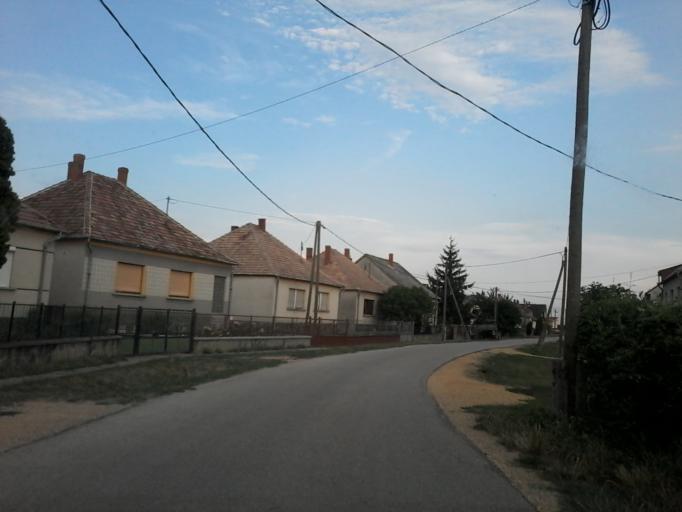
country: HU
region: Vas
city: Sarvar
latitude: 47.2076
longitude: 17.0248
